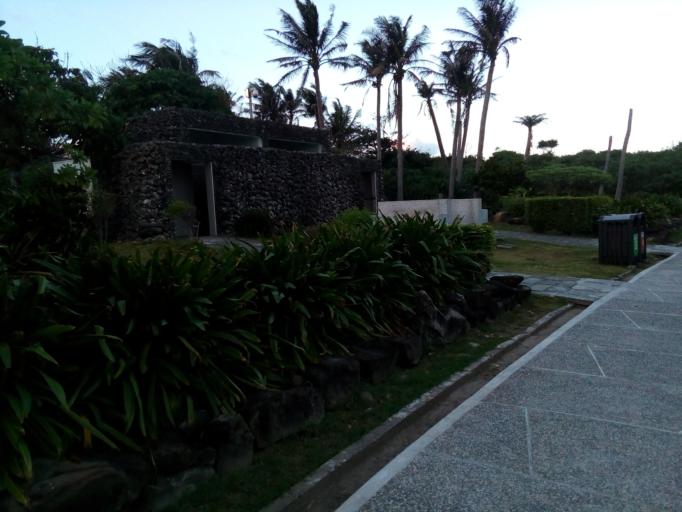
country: TW
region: Taiwan
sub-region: Taitung
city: Taitung
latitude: 22.7957
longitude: 121.1980
